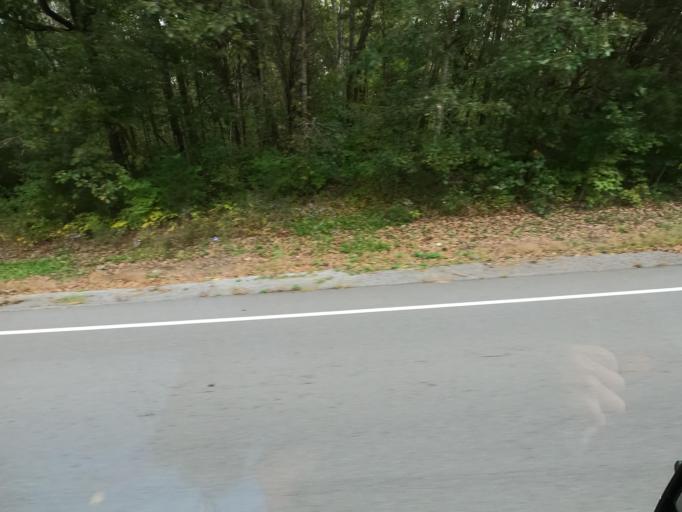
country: US
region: Tennessee
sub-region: Cheatham County
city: Pegram
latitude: 36.0845
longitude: -87.0256
